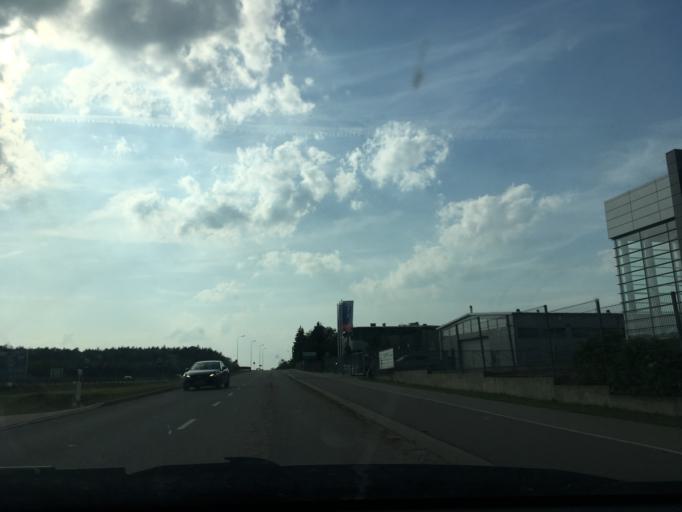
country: PL
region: Podlasie
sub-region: Powiat bialostocki
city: Choroszcz
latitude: 53.1537
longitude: 23.0317
